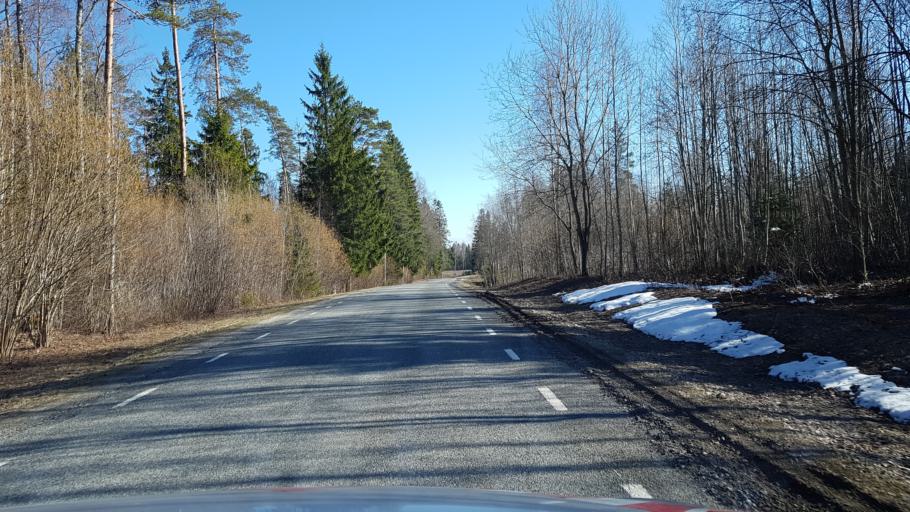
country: EE
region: Laeaene-Virumaa
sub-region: Kadrina vald
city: Kadrina
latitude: 59.3924
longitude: 26.0181
